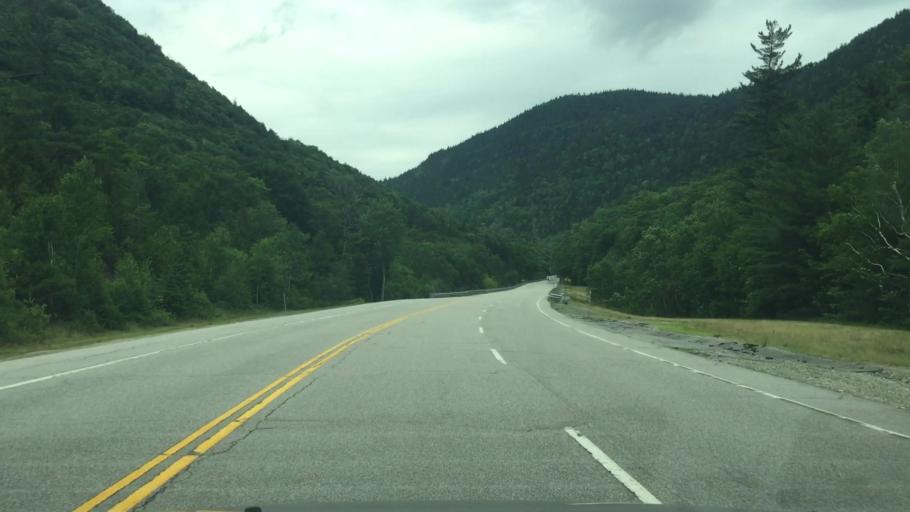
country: US
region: New Hampshire
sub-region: Grafton County
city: Deerfield
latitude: 44.1990
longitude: -71.4070
